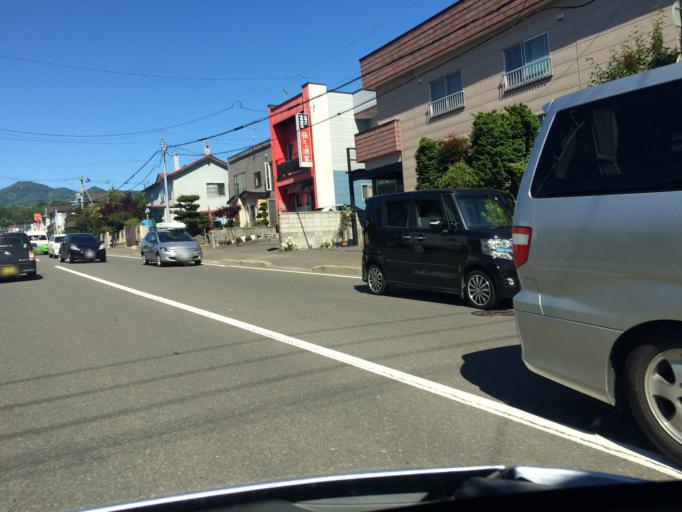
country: JP
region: Hokkaido
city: Sapporo
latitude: 42.9998
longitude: 141.3283
